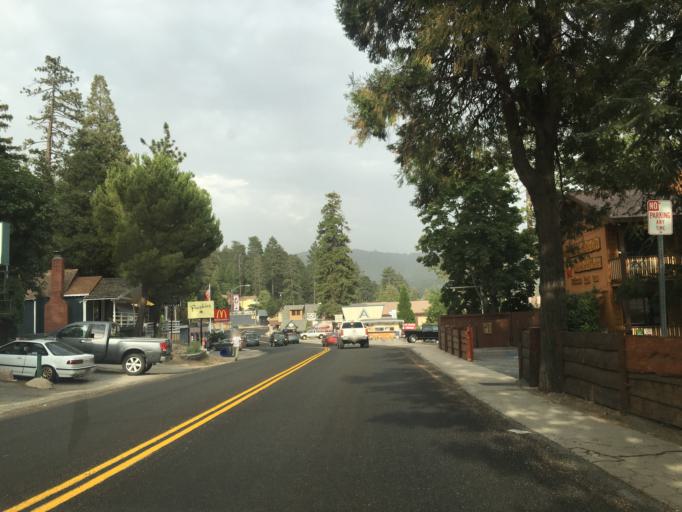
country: US
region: California
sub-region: San Bernardino County
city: Crestline
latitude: 34.2435
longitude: -117.2790
